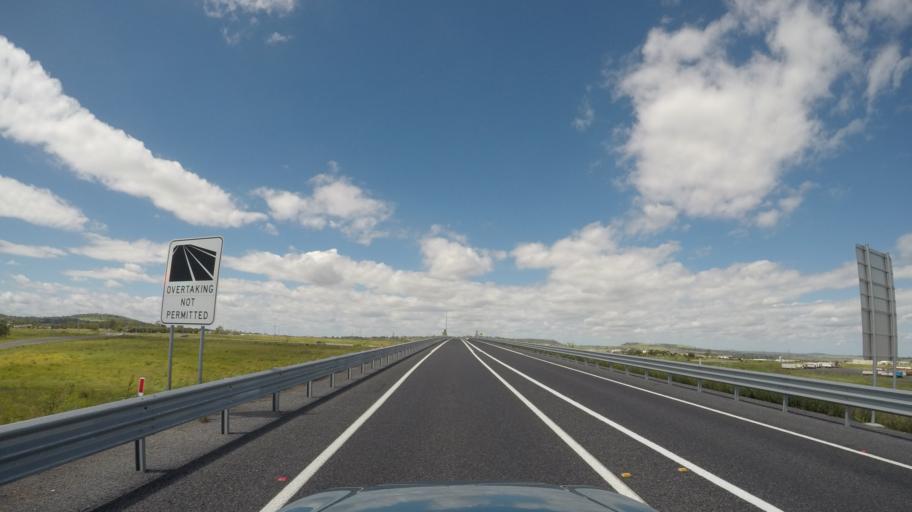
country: AU
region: Queensland
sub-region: Toowoomba
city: Wilsonton Heights
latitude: -27.5224
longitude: 151.8622
